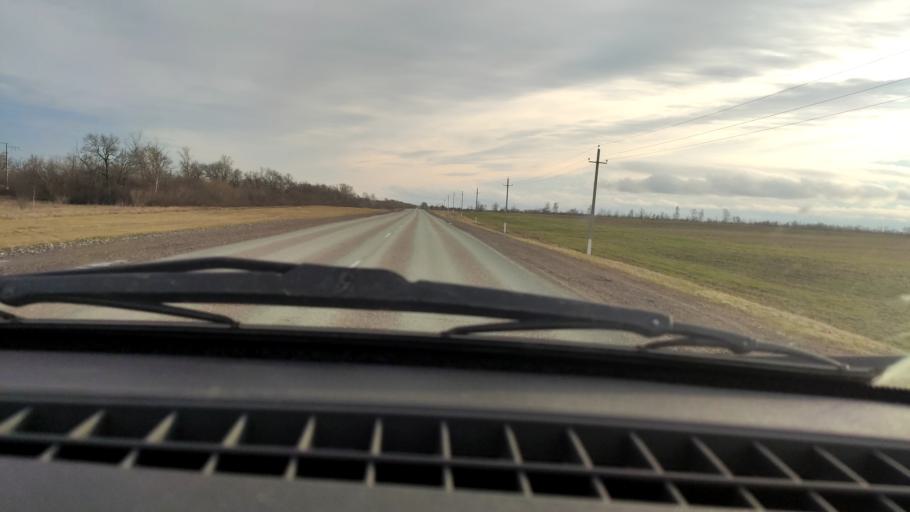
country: RU
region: Bashkortostan
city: Davlekanovo
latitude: 54.3088
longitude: 55.1415
